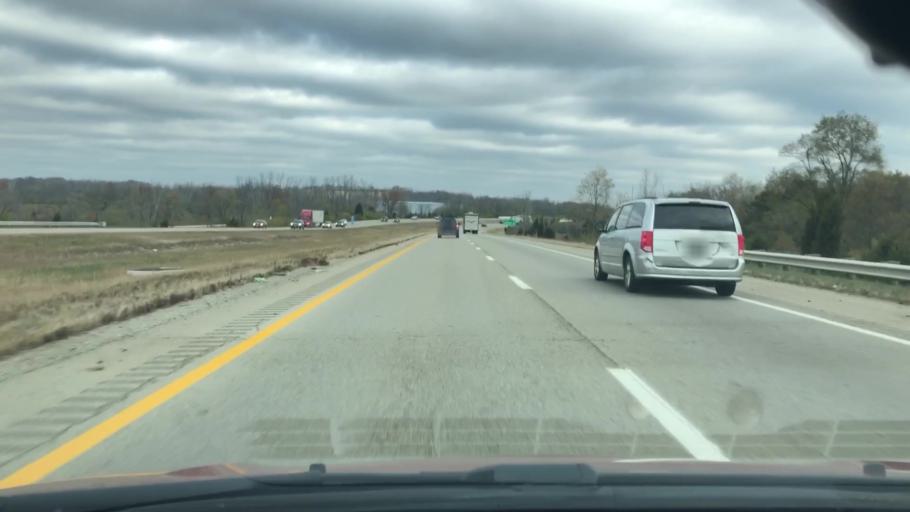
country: US
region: Ohio
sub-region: Greene County
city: Fairborn
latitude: 39.8259
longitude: -83.9999
